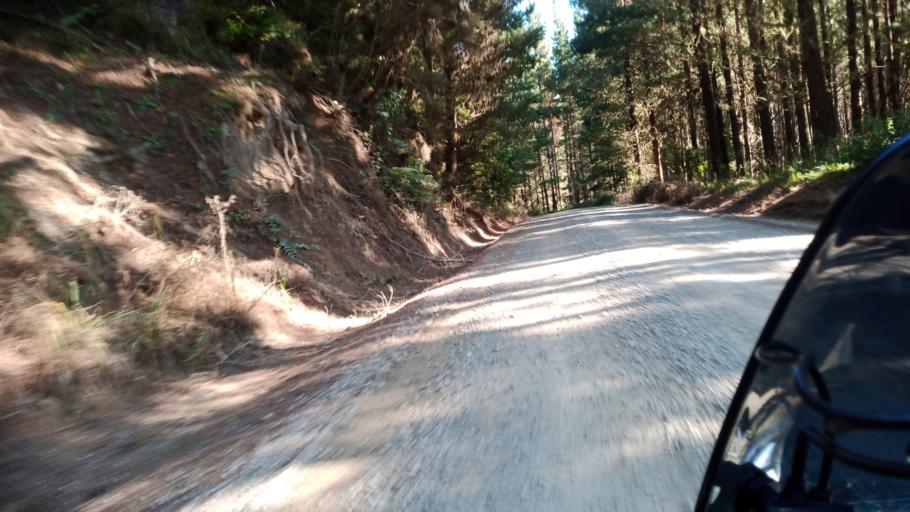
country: NZ
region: Hawke's Bay
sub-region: Wairoa District
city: Wairoa
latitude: -38.9311
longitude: 177.2268
